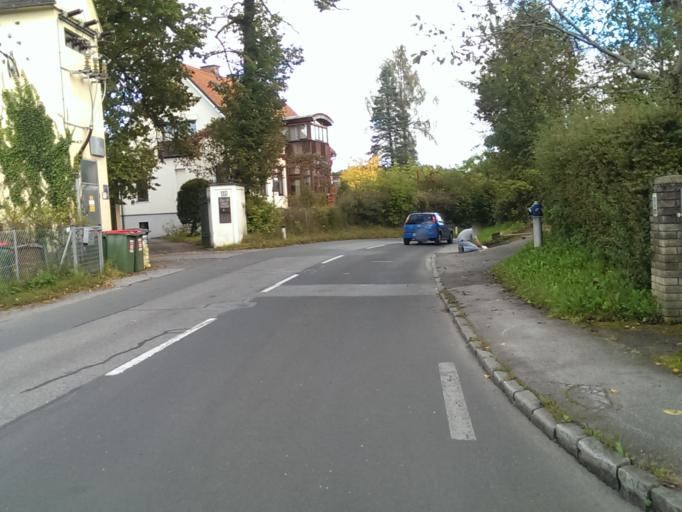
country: AT
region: Styria
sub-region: Politischer Bezirk Graz-Umgebung
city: Hart bei Graz
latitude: 47.0692
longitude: 15.5042
